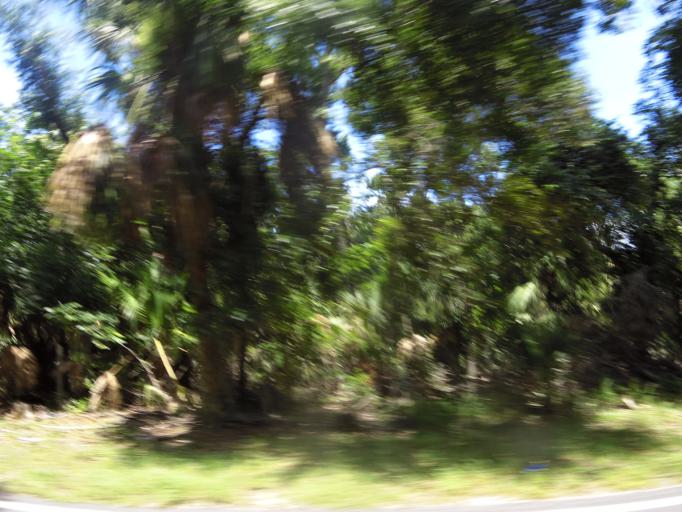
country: US
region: Florida
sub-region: Volusia County
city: Ormond-by-the-Sea
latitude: 29.3761
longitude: -81.1284
